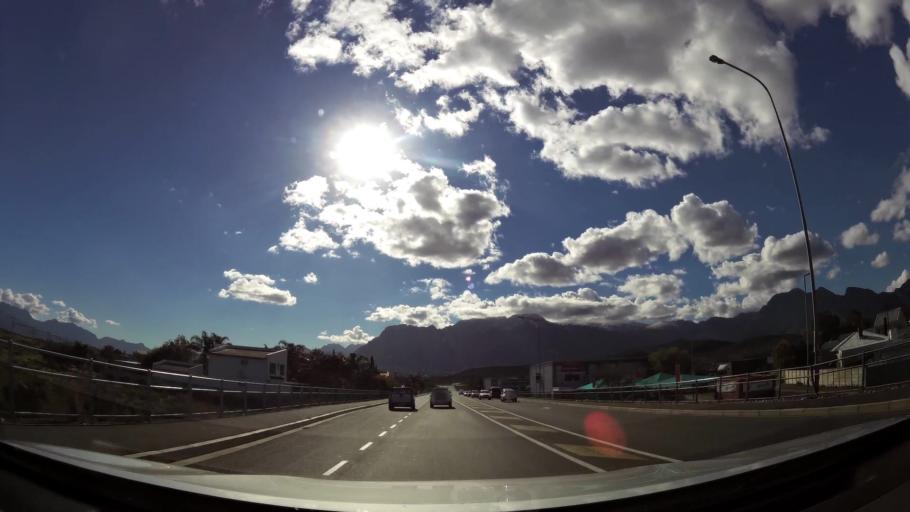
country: ZA
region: Western Cape
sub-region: Cape Winelands District Municipality
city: Worcester
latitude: -33.6397
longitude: 19.4312
